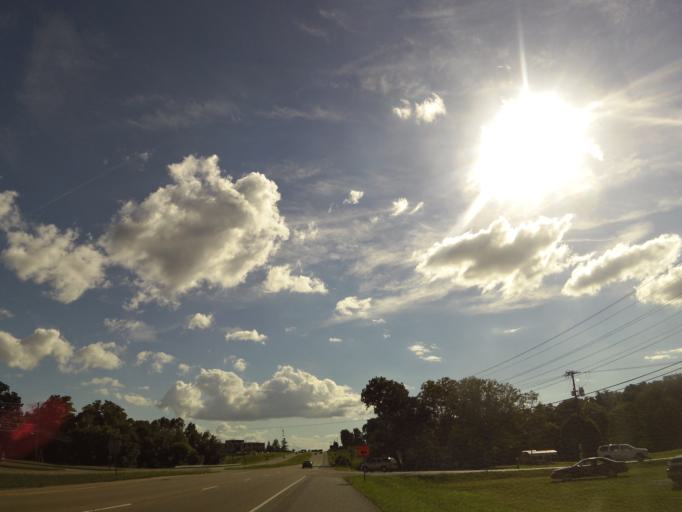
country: US
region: Tennessee
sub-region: Greene County
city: Tusculum
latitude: 36.1884
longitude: -82.7353
